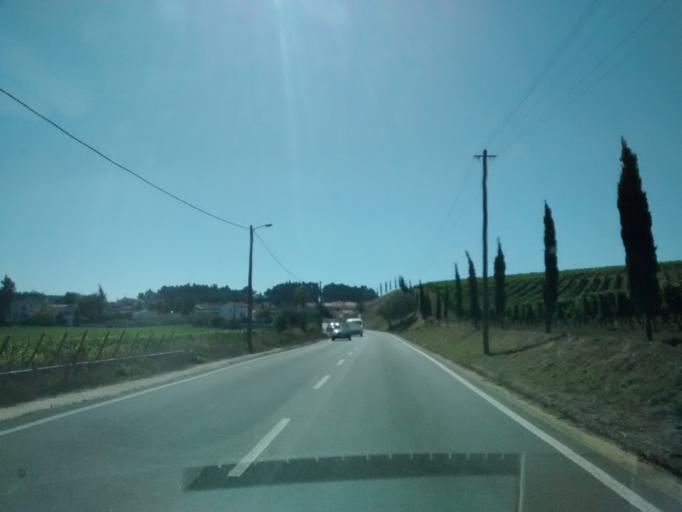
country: PT
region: Aveiro
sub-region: Anadia
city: Arcos
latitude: 40.4393
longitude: -8.4941
